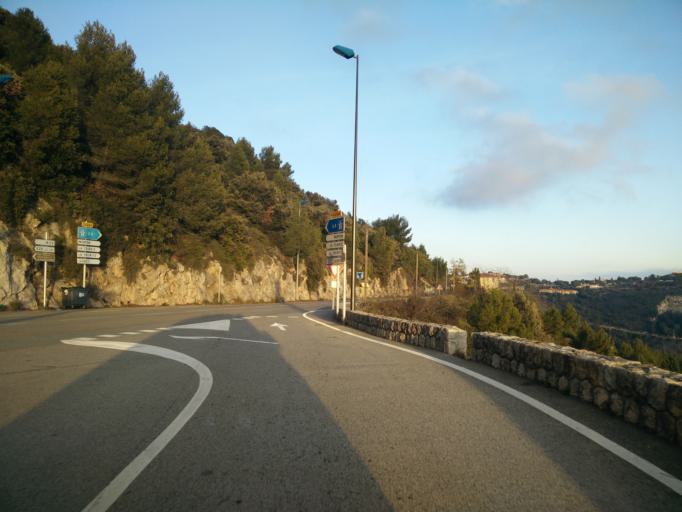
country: FR
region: Provence-Alpes-Cote d'Azur
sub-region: Departement des Alpes-Maritimes
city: La Turbie
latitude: 43.7381
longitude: 7.3865
